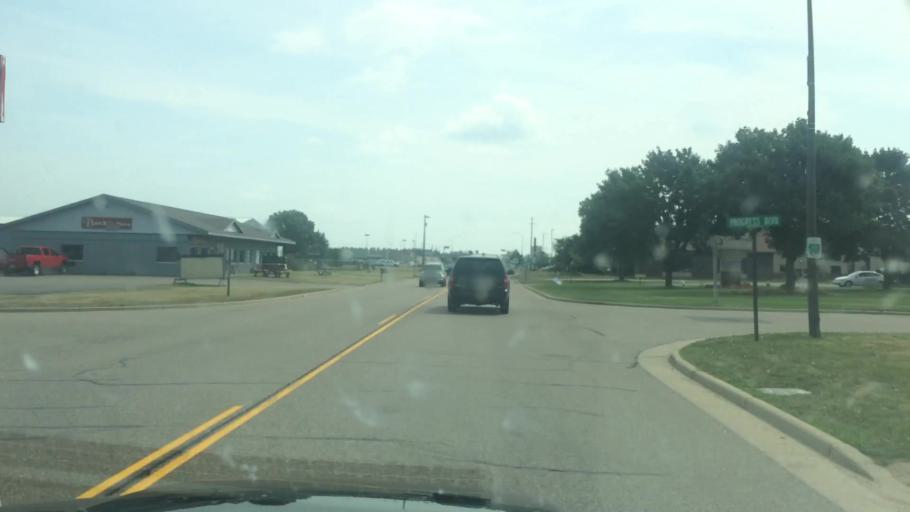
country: US
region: Wisconsin
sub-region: Langlade County
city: Antigo
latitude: 45.1621
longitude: -89.1516
